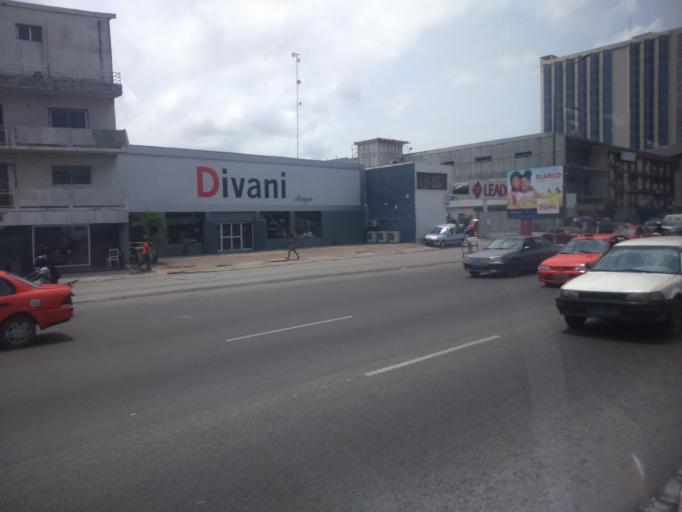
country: CI
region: Lagunes
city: Abidjan
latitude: 5.2998
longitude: -3.9883
